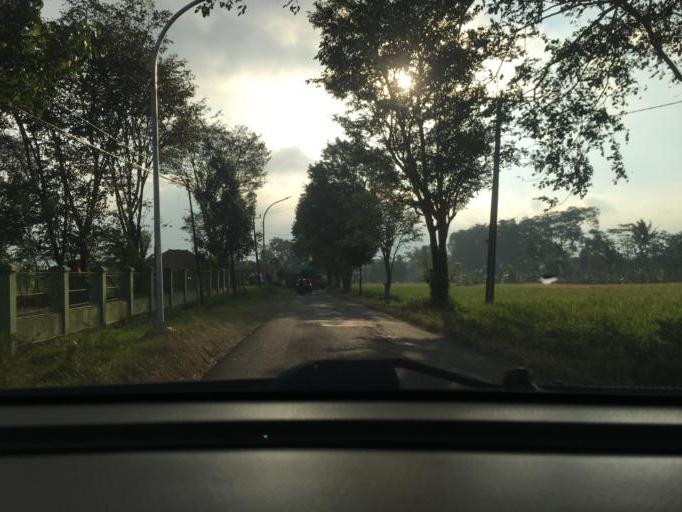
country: ID
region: West Java
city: Rawa
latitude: -7.0316
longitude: 108.3405
